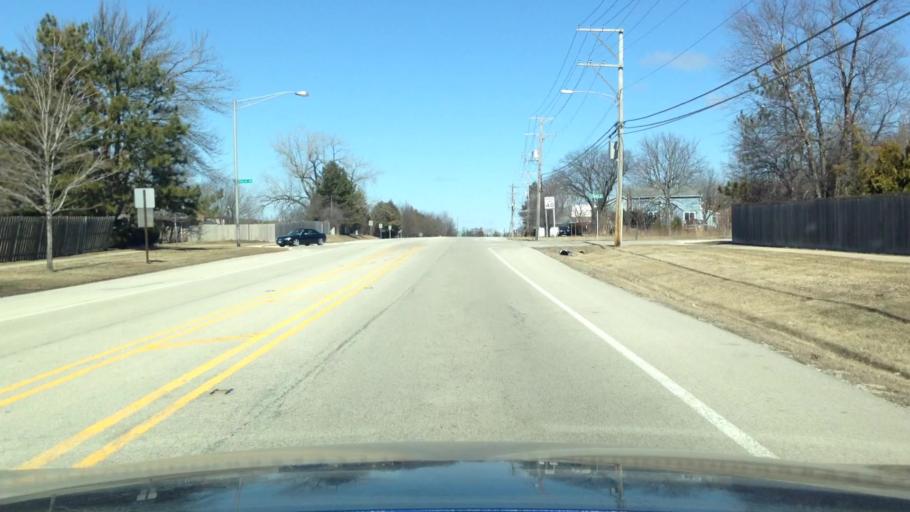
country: US
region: Illinois
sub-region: Lake County
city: Riverwoods
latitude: 42.1488
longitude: -87.8830
